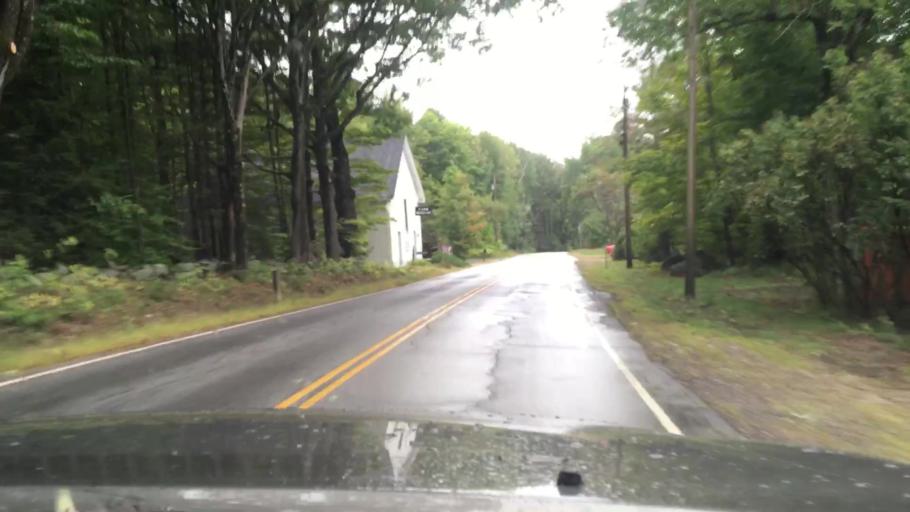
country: US
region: New Hampshire
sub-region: Belknap County
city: Meredith
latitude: 43.6464
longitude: -71.5374
